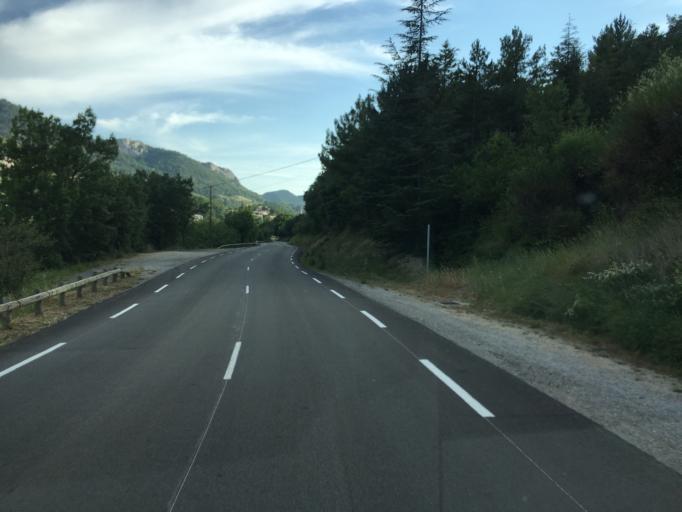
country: FR
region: Rhone-Alpes
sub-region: Departement de la Drome
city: Buis-les-Baronnies
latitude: 44.4186
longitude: 5.2724
